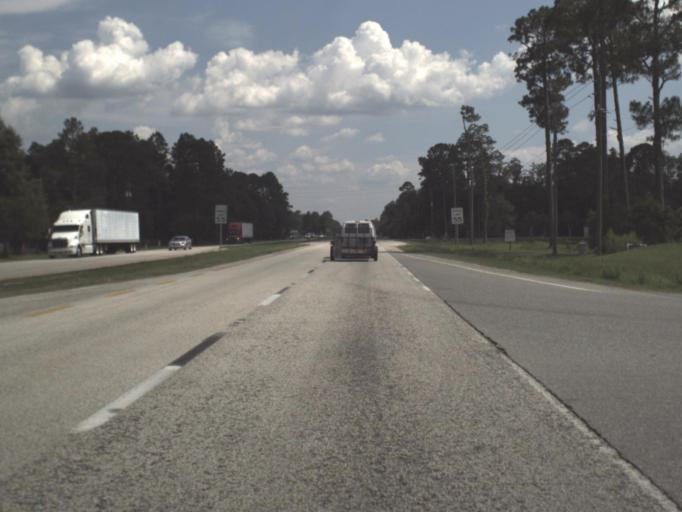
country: US
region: Florida
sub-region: Alachua County
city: Waldo
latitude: 29.8137
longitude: -82.1678
